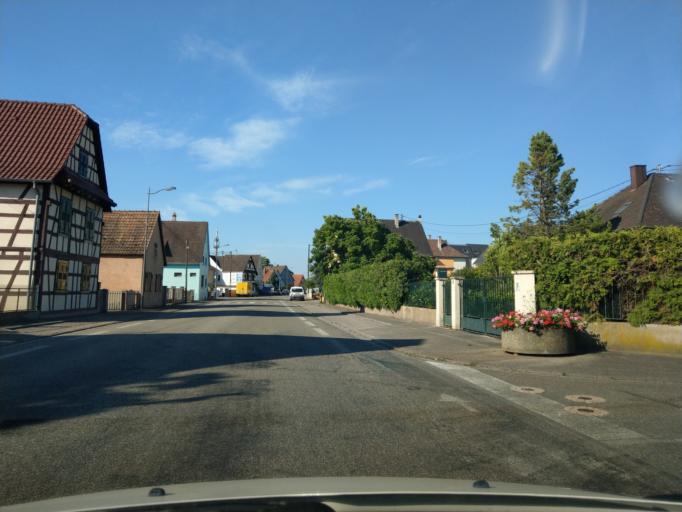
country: FR
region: Alsace
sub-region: Departement du Bas-Rhin
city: Herrlisheim
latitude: 48.7272
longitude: 7.9051
